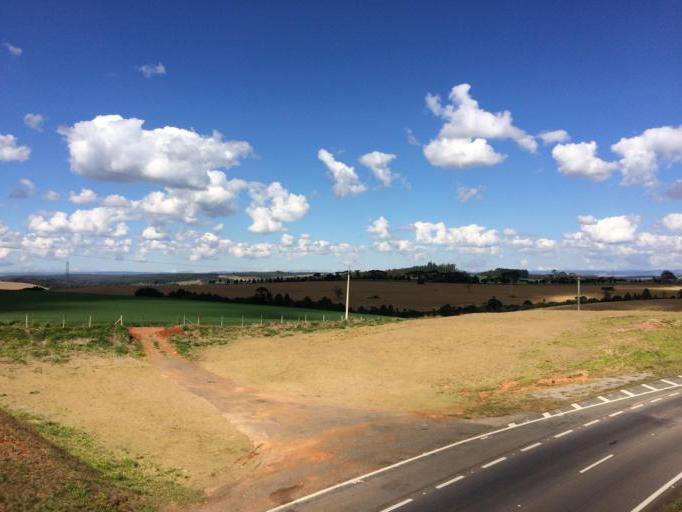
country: BR
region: Sao Paulo
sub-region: Capao Bonito
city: Capao Bonito
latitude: -23.9044
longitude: -48.2714
